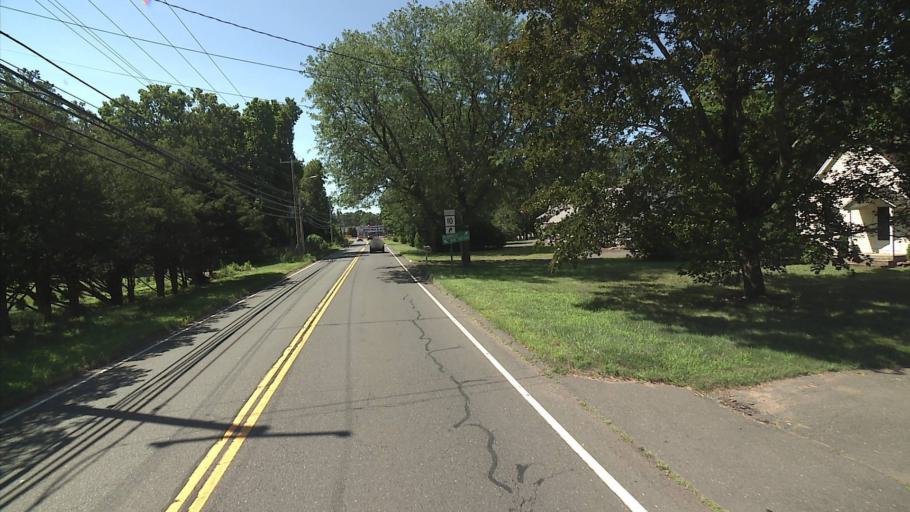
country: US
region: Connecticut
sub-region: Hartford County
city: Farmington
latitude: 41.6996
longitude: -72.8443
